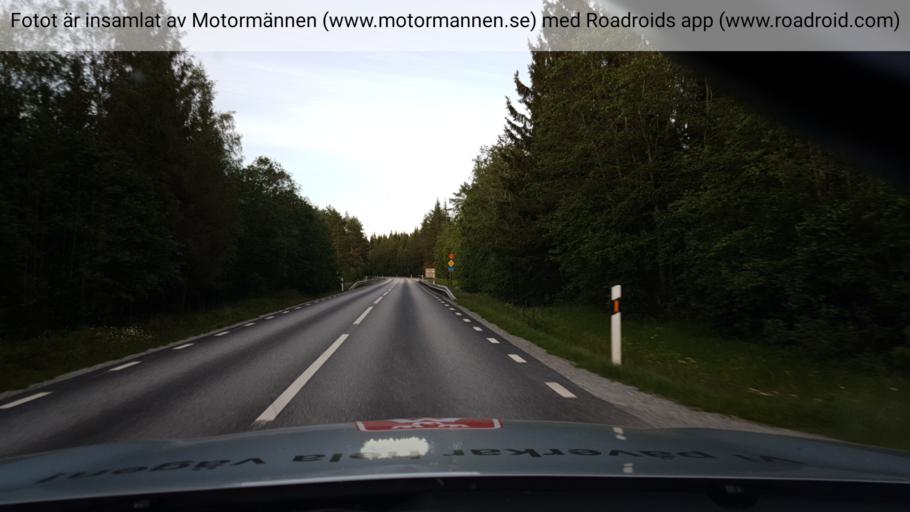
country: SE
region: Vaestmanland
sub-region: Skinnskattebergs Kommun
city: Skinnskatteberg
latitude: 59.7731
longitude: 15.5339
